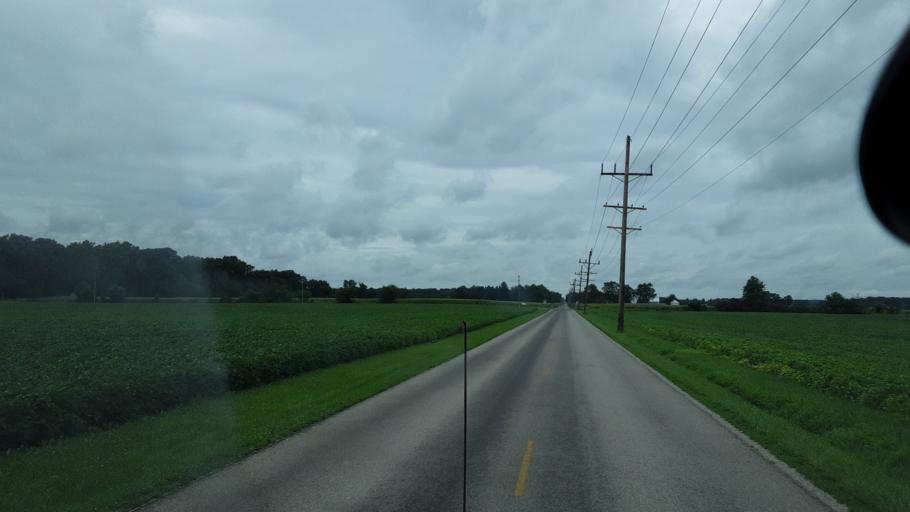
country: US
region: Indiana
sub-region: Jay County
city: Portland
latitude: 40.4439
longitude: -85.0199
